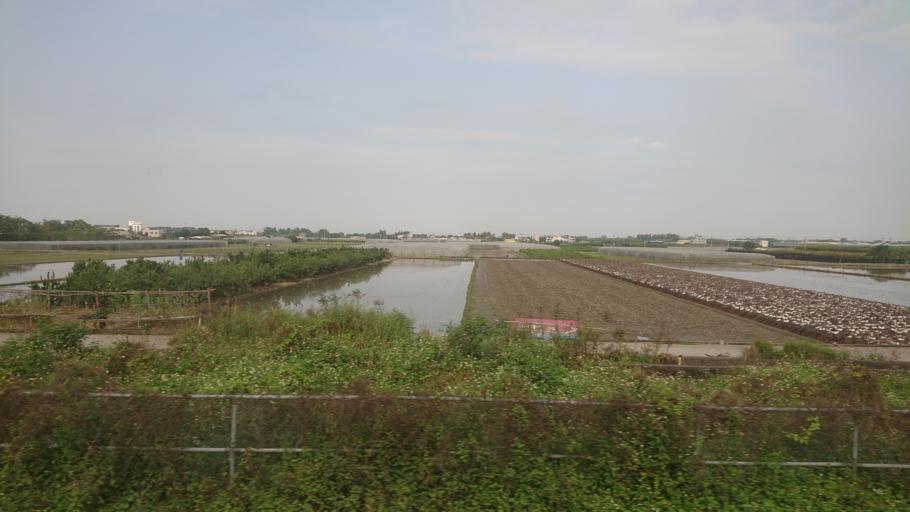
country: TW
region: Taiwan
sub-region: Yunlin
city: Douliu
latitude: 23.7300
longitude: 120.5779
